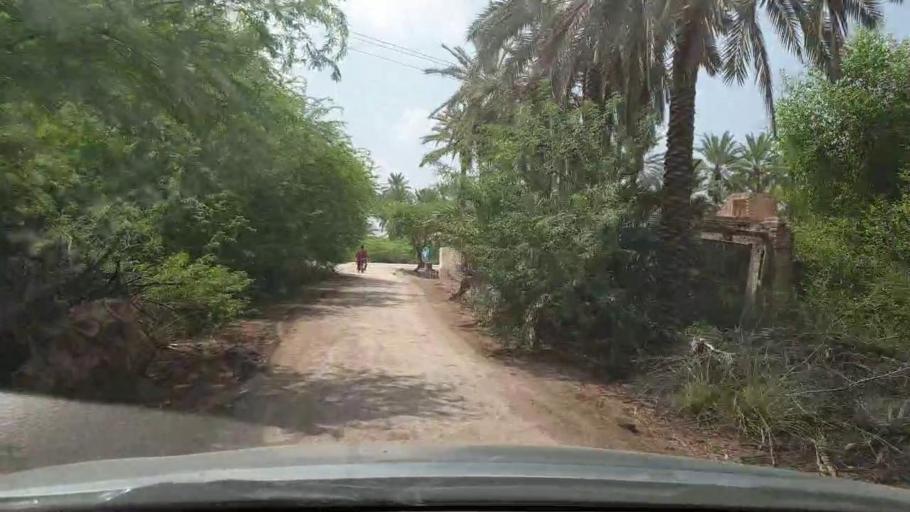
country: PK
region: Sindh
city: Kot Diji
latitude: 27.4070
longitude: 68.7454
